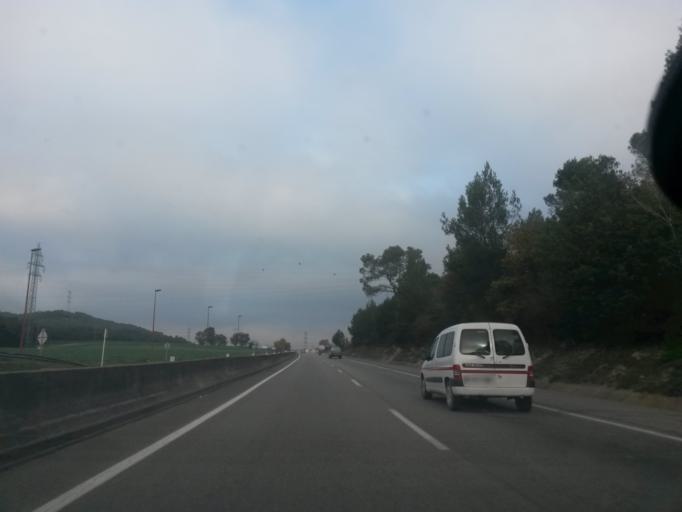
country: ES
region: Catalonia
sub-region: Provincia de Girona
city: Sarria de Ter
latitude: 42.0426
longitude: 2.8214
